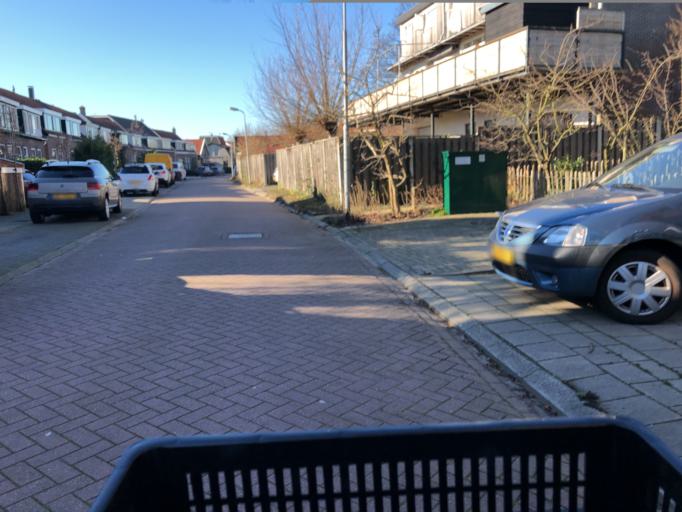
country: NL
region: North Holland
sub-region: Gemeente Zaanstad
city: Zaanstad
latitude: 52.4306
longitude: 4.7817
